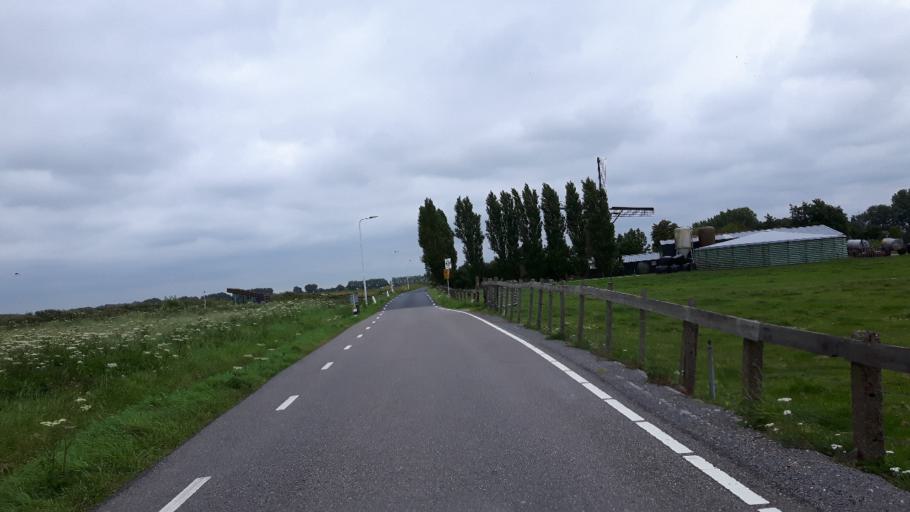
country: NL
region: South Holland
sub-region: Gemeente Pijnacker-Nootdorp
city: Pijnacker
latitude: 51.9814
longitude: 4.4275
